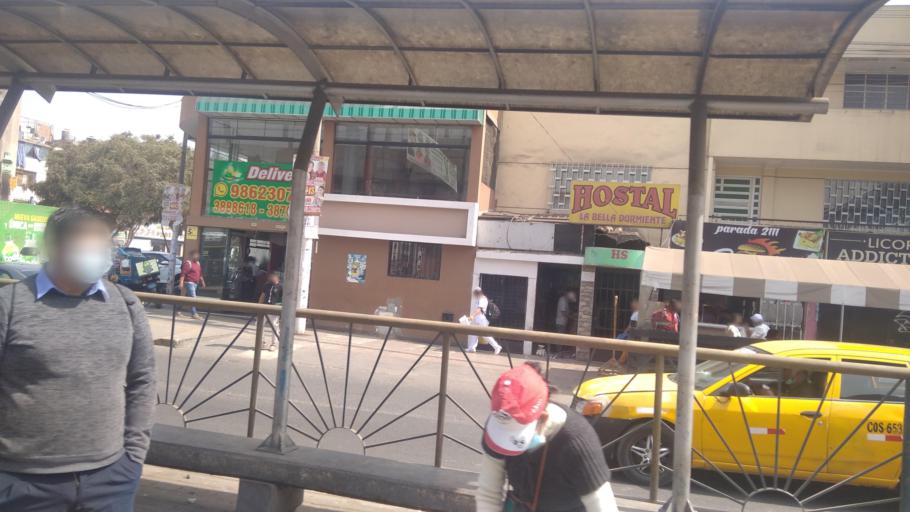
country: PE
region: Lima
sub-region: Lima
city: Independencia
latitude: -11.9969
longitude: -77.0100
